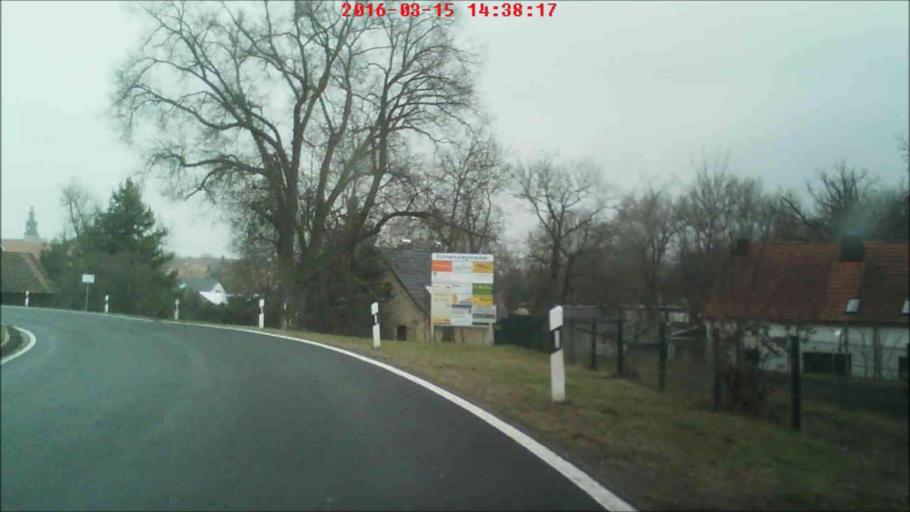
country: DE
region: Thuringia
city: Elxleben
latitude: 50.8735
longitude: 11.0520
